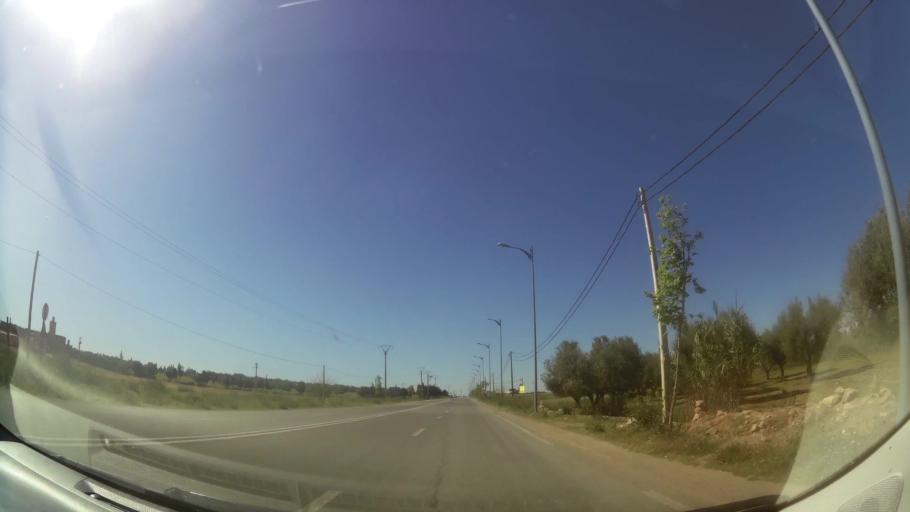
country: MA
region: Oriental
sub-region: Oujda-Angad
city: Oujda
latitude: 34.7211
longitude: -1.8658
